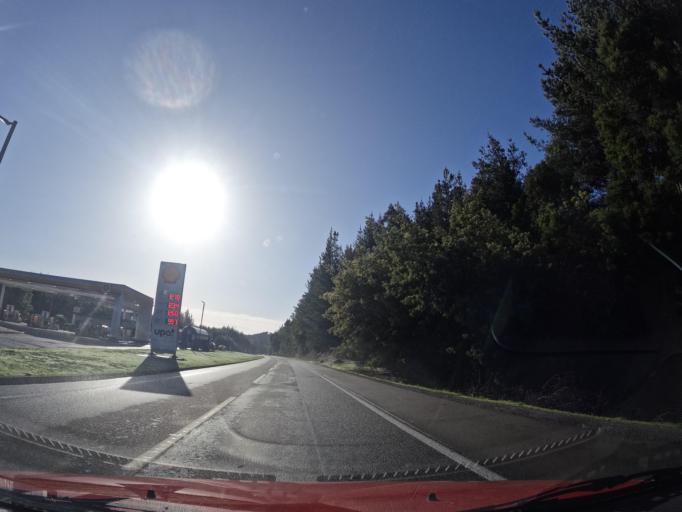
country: CL
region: Biobio
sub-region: Provincia de Concepcion
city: Penco
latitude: -36.7480
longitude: -72.9191
